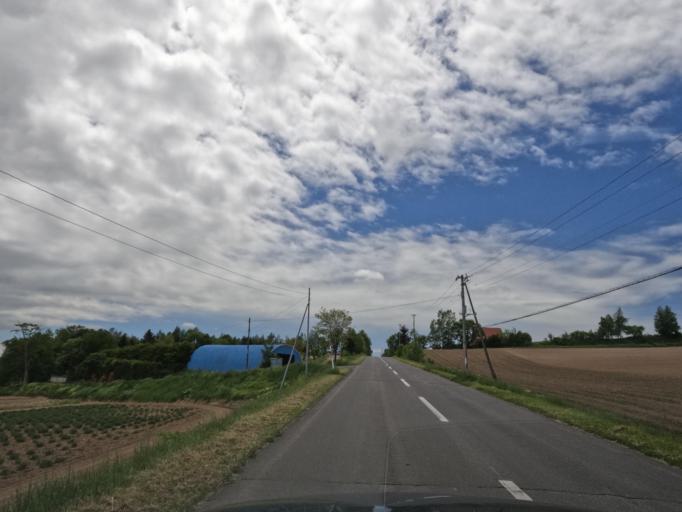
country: JP
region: Hokkaido
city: Shimo-furano
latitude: 43.5236
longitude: 142.4332
